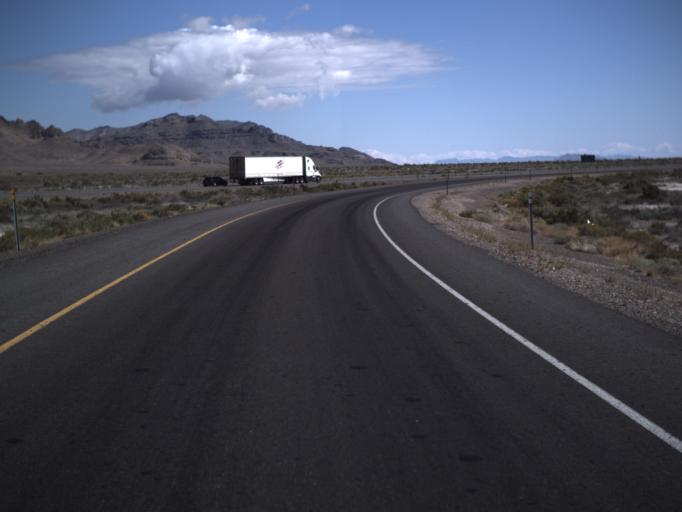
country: US
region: Utah
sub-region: Tooele County
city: Wendover
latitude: 40.7447
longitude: -114.0169
